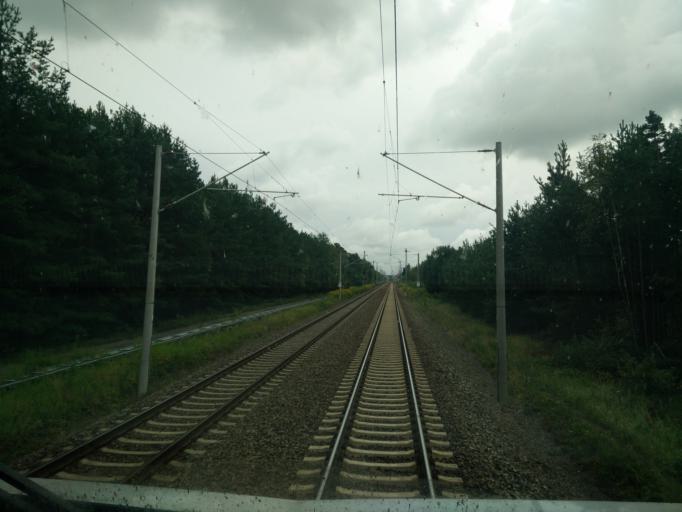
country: DE
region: Brandenburg
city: Halbe
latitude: 52.1204
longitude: 13.6890
